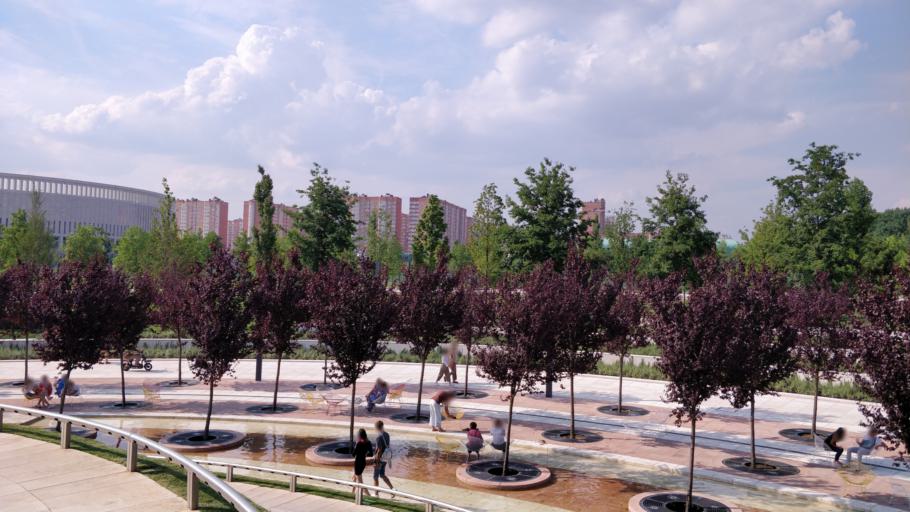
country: RU
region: Krasnodarskiy
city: Krasnodar
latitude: 45.0414
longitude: 39.0336
